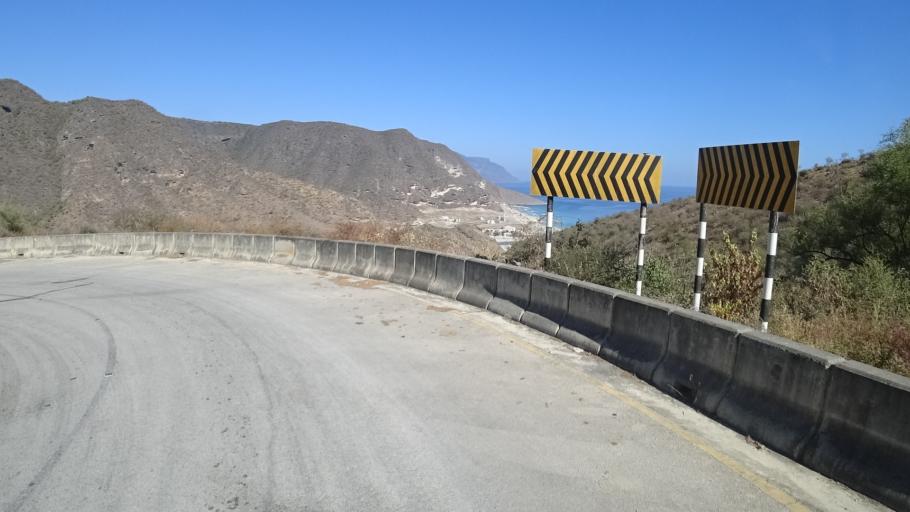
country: YE
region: Al Mahrah
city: Hawf
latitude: 16.7469
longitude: 53.4093
